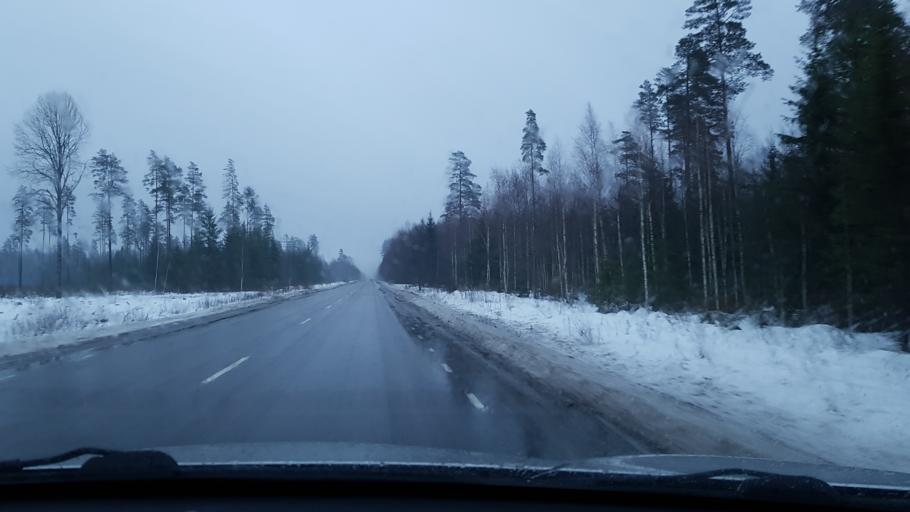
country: EE
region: Paernumaa
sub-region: Vaendra vald (alev)
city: Vandra
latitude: 58.8177
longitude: 25.1605
